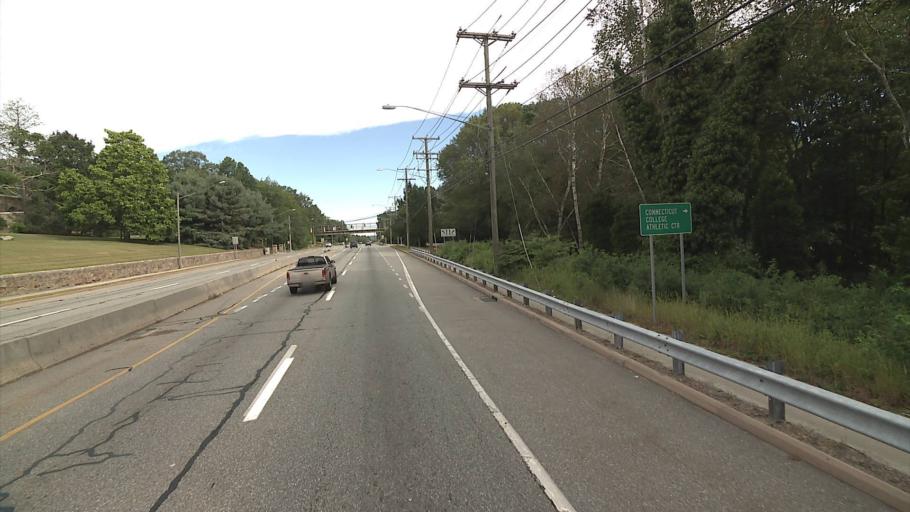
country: US
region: Connecticut
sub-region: New London County
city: New London
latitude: 41.3794
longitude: -72.1039
